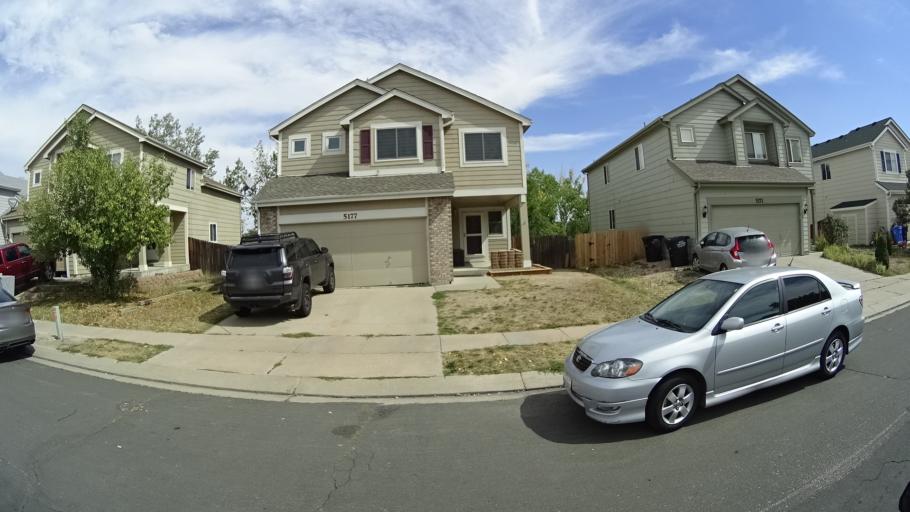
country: US
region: Colorado
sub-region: El Paso County
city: Cimarron Hills
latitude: 38.9051
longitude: -104.7083
